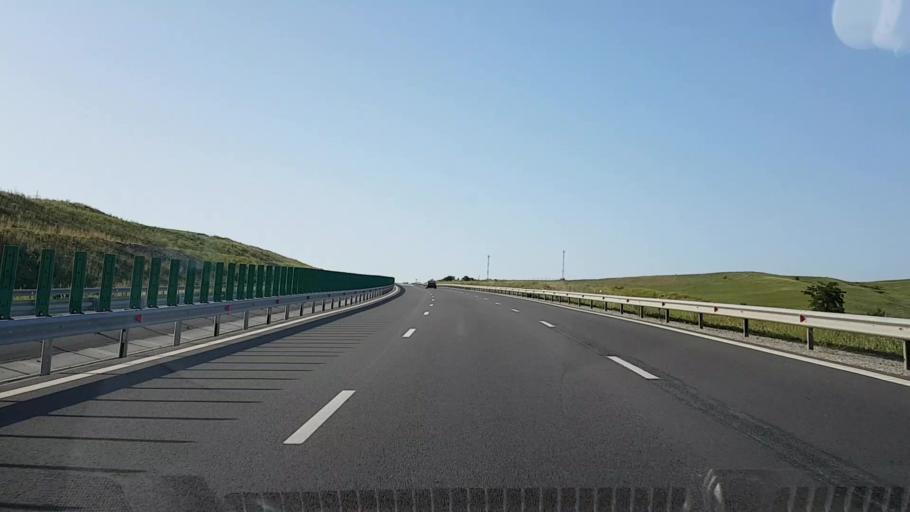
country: RO
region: Cluj
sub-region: Comuna Mihai Viteazu
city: Mihai Viteazu
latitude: 46.4947
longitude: 23.7810
